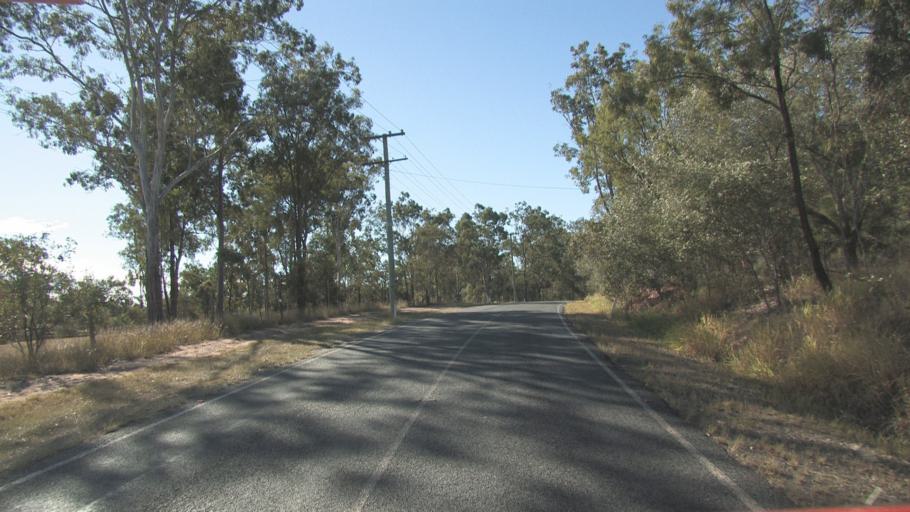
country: AU
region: Queensland
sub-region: Logan
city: Cedar Vale
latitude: -27.8254
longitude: 153.0540
